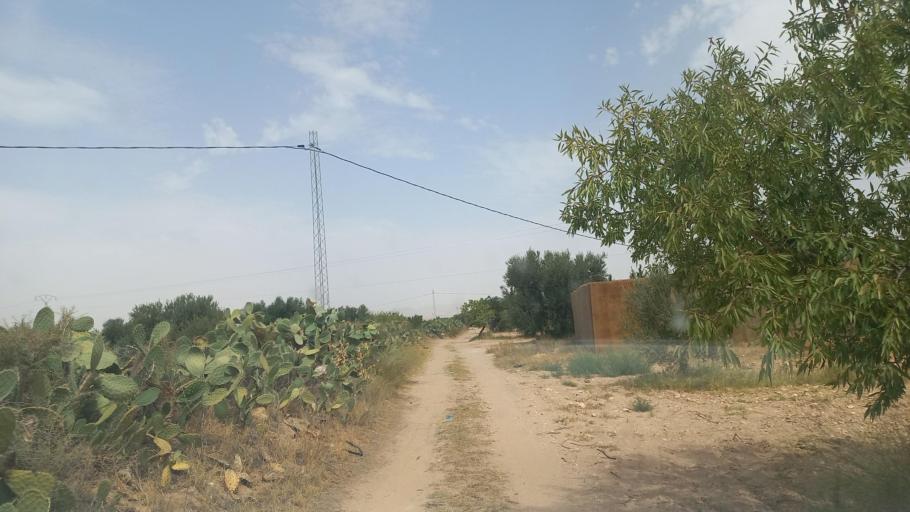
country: TN
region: Al Qasrayn
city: Kasserine
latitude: 35.2597
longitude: 8.9998
